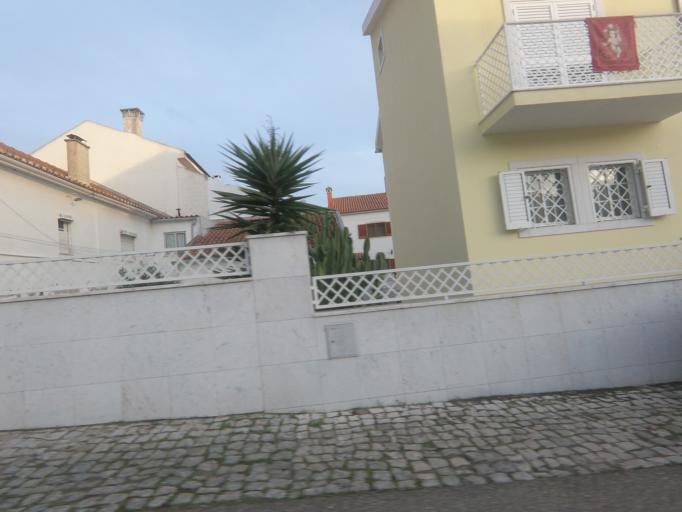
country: PT
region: Setubal
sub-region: Setubal
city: Setubal
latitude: 38.5269
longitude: -8.8620
